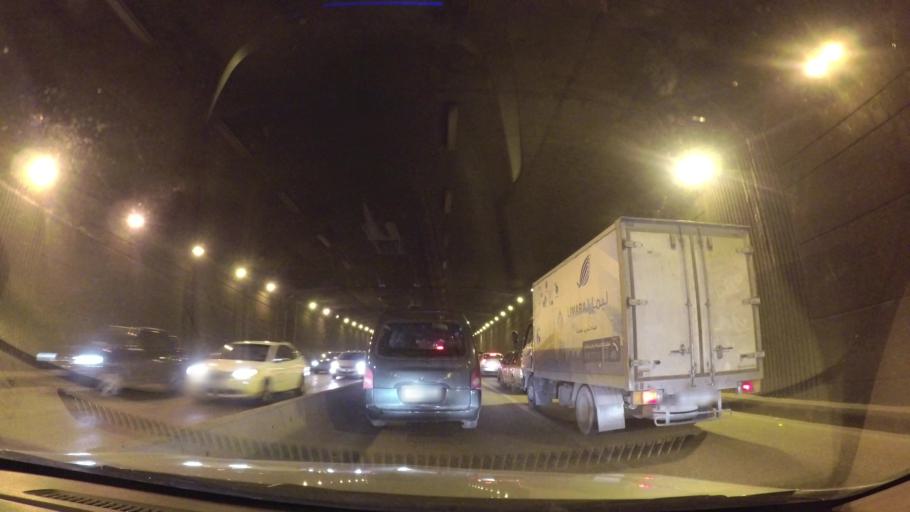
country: JO
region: Amman
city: Al Bunayyat ash Shamaliyah
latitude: 31.9468
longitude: 35.8909
